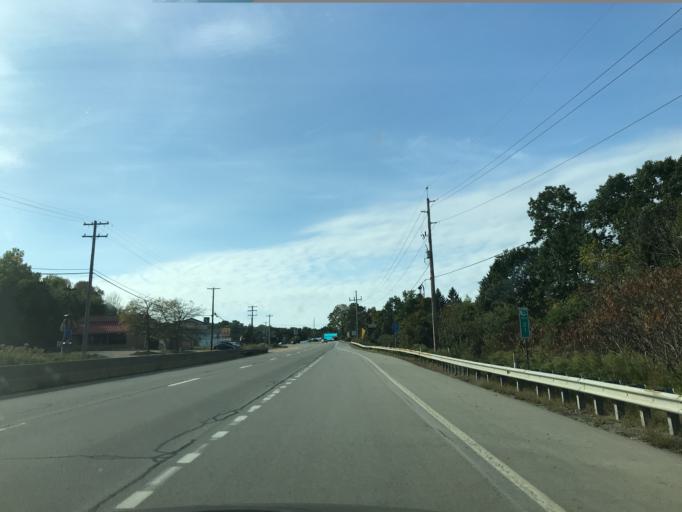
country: US
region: Pennsylvania
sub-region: Crawford County
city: Meadville
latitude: 41.6242
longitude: -80.1876
